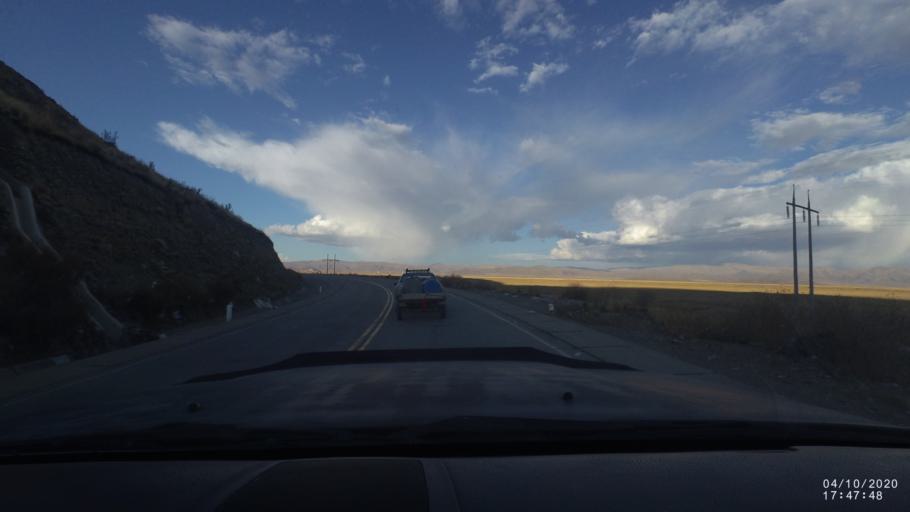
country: BO
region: Oruro
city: Oruro
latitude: -18.0227
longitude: -67.1408
